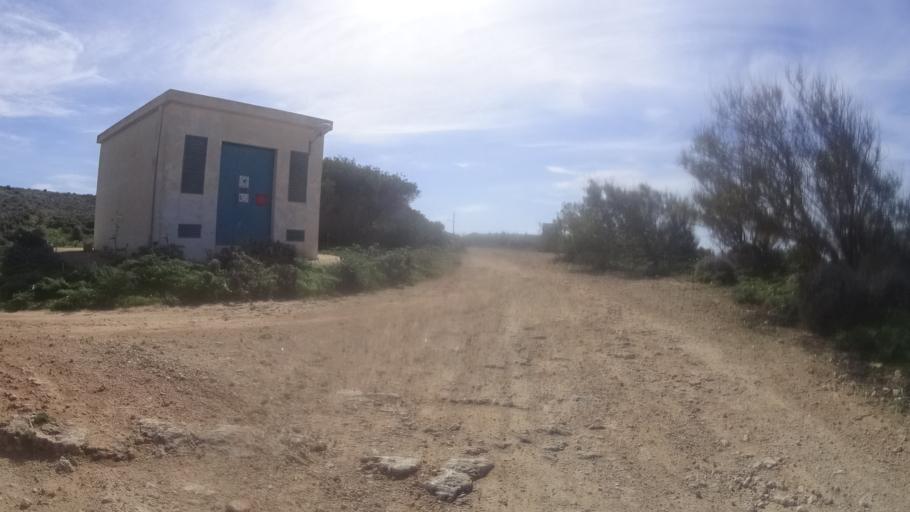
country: MT
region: Il-Qala
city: Qala
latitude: 36.0115
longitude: 14.3323
